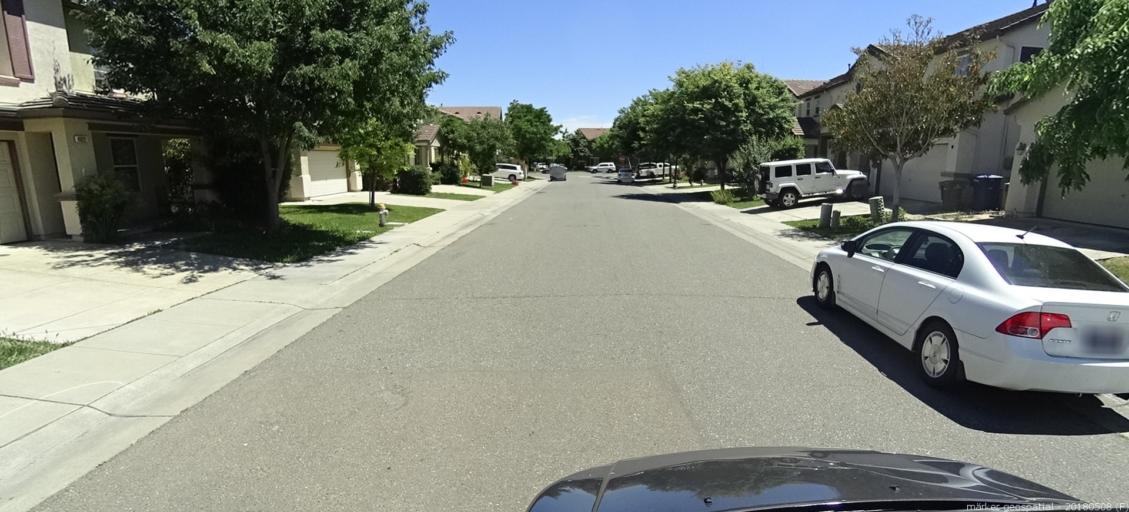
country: US
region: California
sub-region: Yolo County
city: West Sacramento
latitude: 38.6613
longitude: -121.5258
